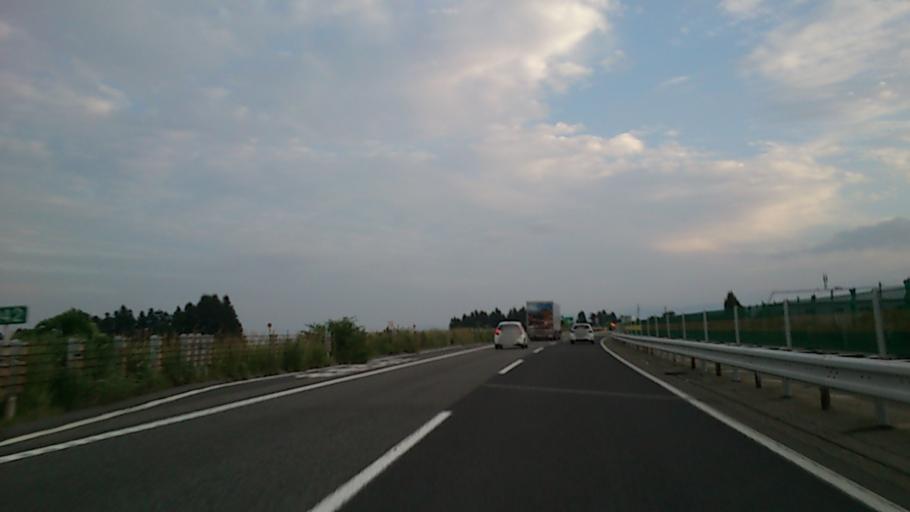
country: JP
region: Nagano
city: Iida
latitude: 35.5612
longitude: 137.8610
